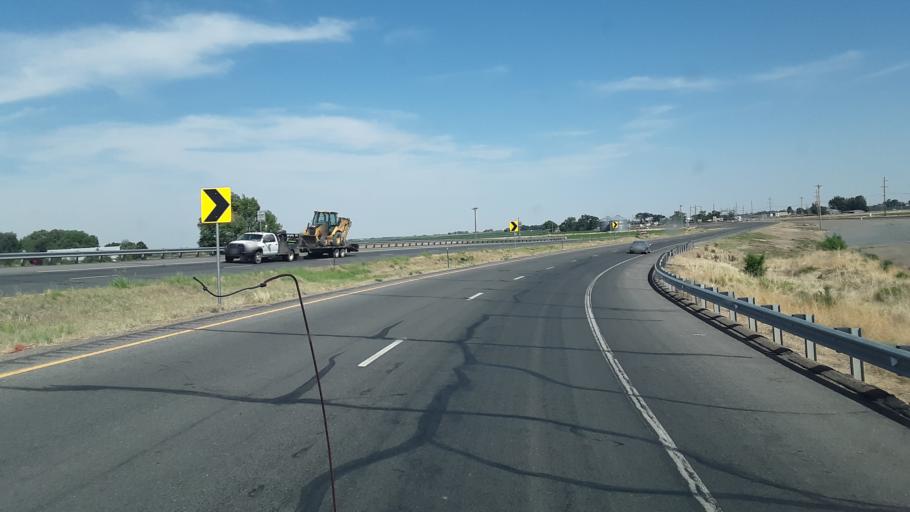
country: US
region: Colorado
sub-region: Otero County
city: Rocky Ford
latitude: 38.1028
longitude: -103.8407
